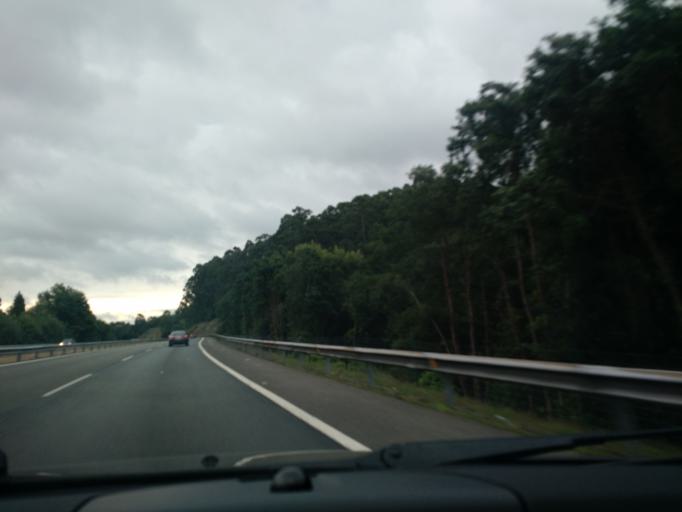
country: ES
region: Galicia
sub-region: Provincia da Coruna
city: Cambre
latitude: 43.3053
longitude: -8.3370
